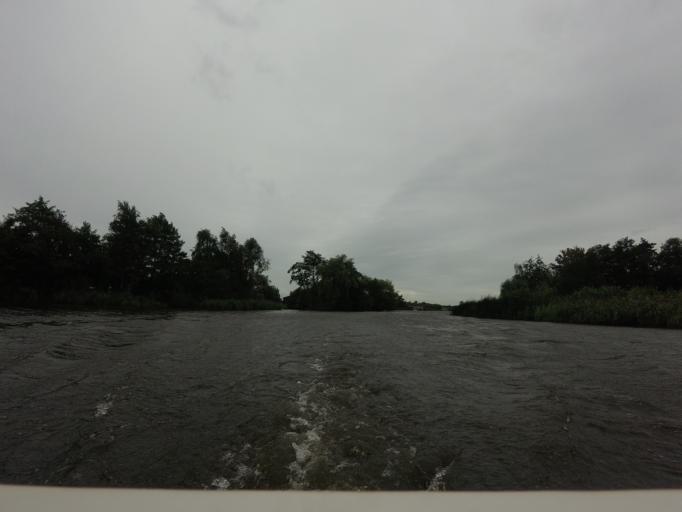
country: NL
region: Friesland
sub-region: Gemeente Boarnsterhim
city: Warten
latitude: 53.1258
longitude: 5.9318
